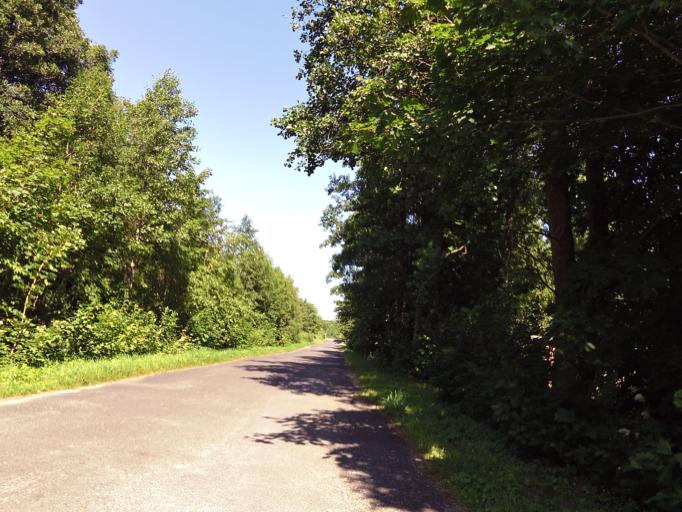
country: EE
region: Hiiumaa
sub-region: Kaerdla linn
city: Kardla
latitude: 58.7830
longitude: 22.4911
